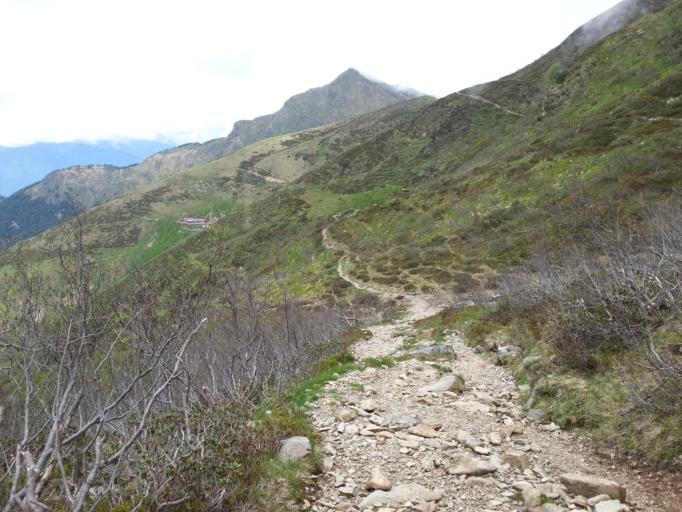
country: IT
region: Lombardy
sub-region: Provincia di Varese
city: Curiglia
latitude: 46.0836
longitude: 8.8606
